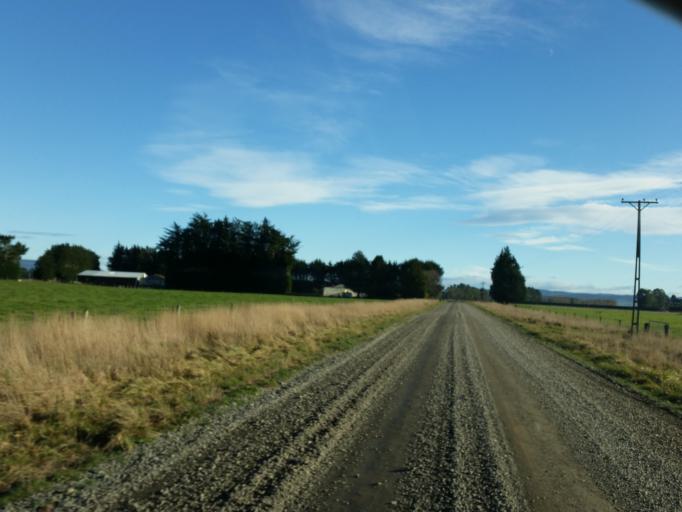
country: NZ
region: Southland
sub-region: Southland District
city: Winton
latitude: -46.0953
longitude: 168.1040
